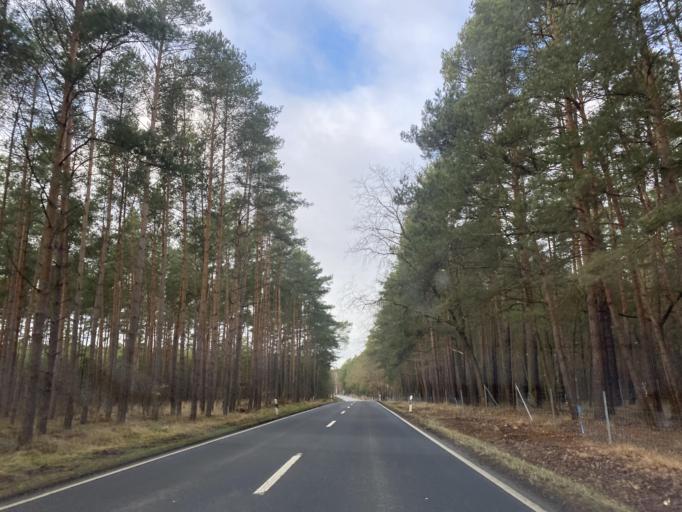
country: PL
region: Lubusz
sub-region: Powiat zarski
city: Leknica
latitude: 51.5047
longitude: 14.8009
